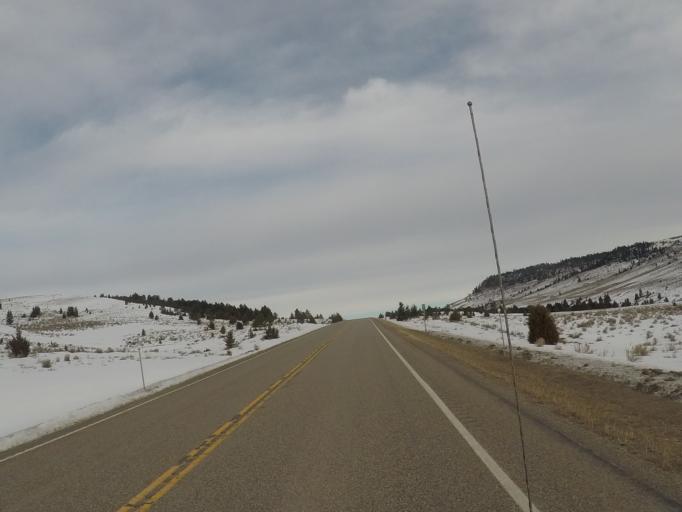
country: US
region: Montana
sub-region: Meagher County
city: White Sulphur Springs
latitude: 46.6399
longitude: -110.8743
